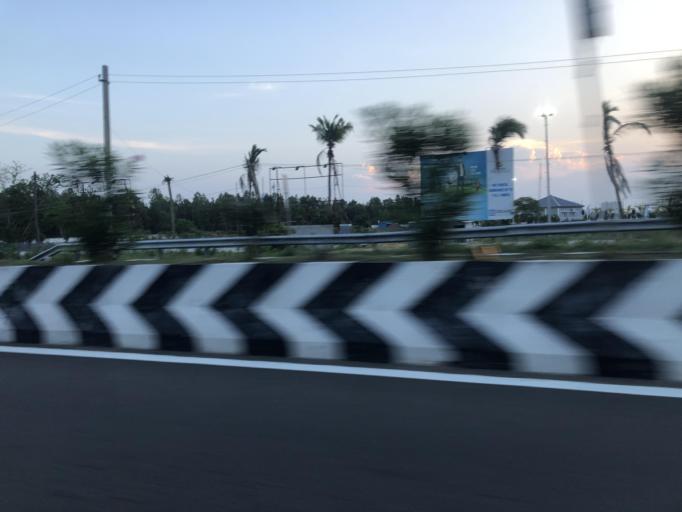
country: IN
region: Tamil Nadu
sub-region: Kancheepuram
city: Injambakkam
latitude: 12.7892
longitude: 80.2430
